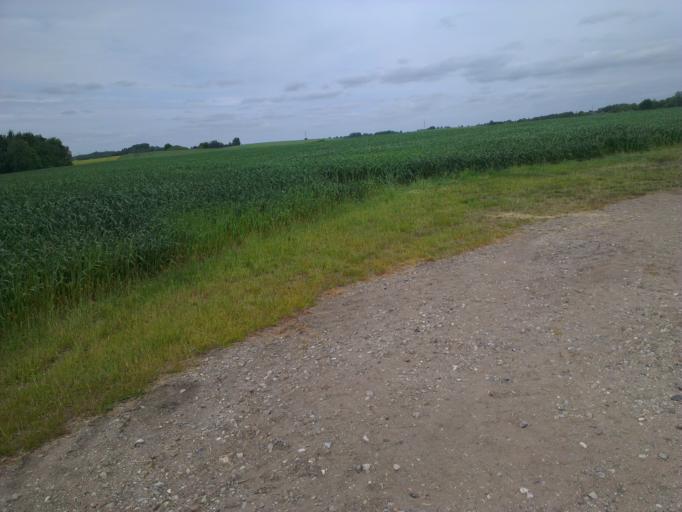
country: DK
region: Capital Region
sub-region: Frederikssund Kommune
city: Frederikssund
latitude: 55.8274
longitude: 12.1065
